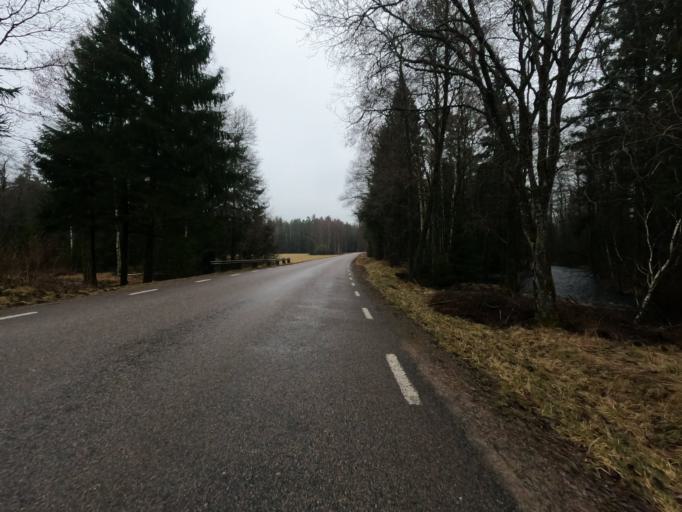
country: SE
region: Halland
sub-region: Hylte Kommun
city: Torup
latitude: 56.7942
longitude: 13.1941
